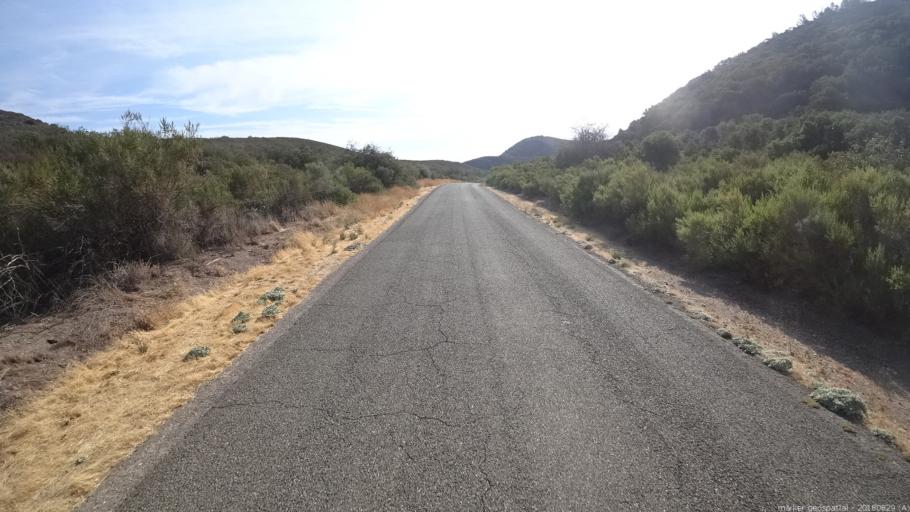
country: US
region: California
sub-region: Monterey County
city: King City
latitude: 36.0456
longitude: -121.0678
